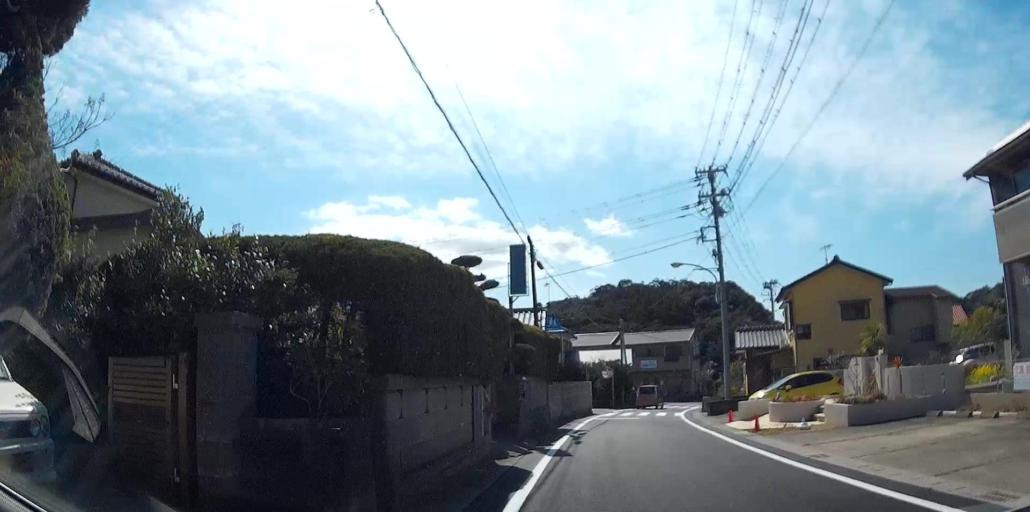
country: JP
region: Chiba
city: Tateyama
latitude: 35.0358
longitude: 139.8510
